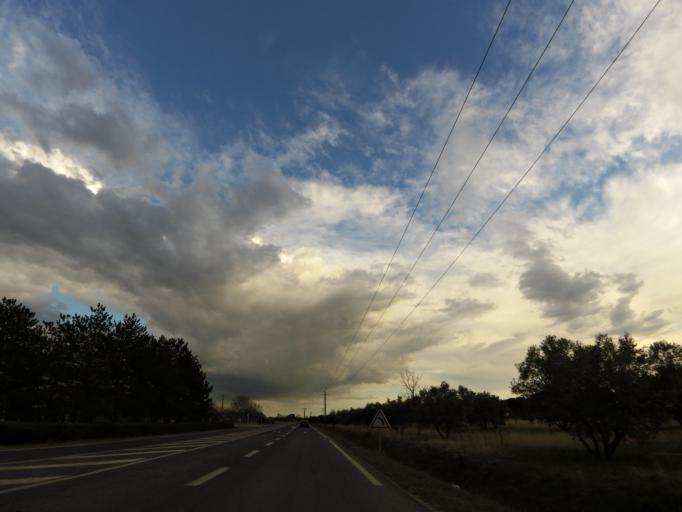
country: FR
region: Languedoc-Roussillon
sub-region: Departement du Gard
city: Codognan
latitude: 43.7287
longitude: 4.2401
